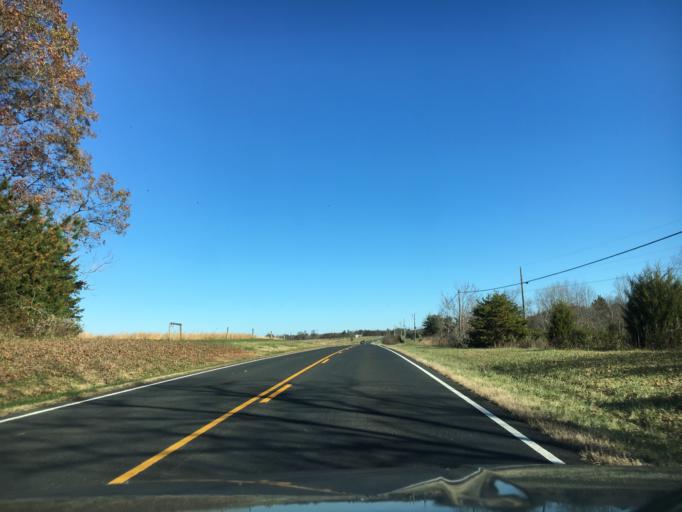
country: US
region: Virginia
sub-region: Appomattox County
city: Appomattox
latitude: 37.4002
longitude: -78.7734
